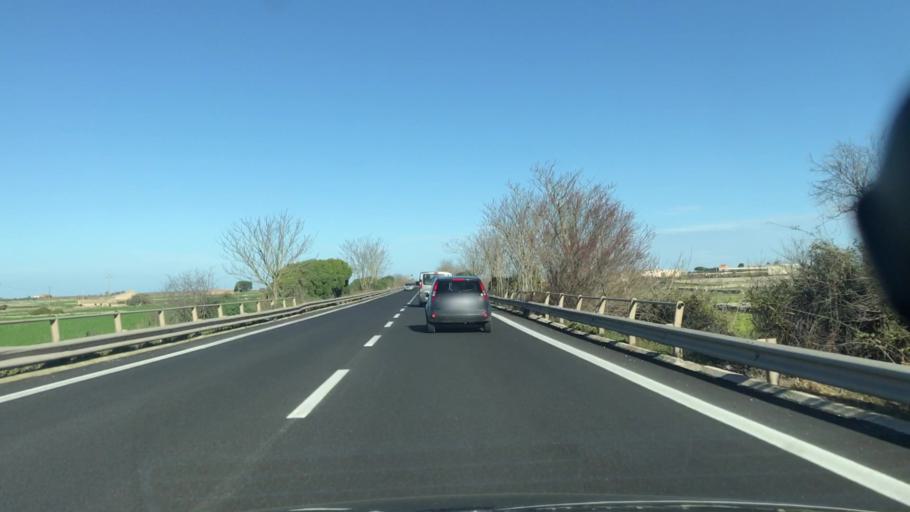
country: IT
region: Sicily
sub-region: Ragusa
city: Ragusa
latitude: 36.9261
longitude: 14.6654
